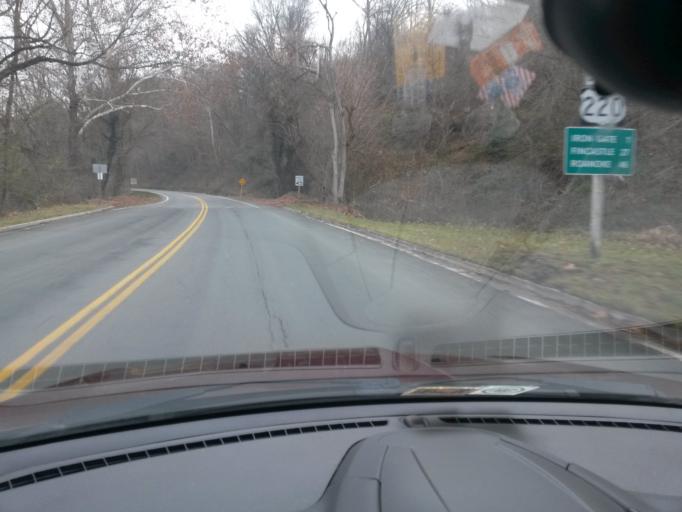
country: US
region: Virginia
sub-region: Alleghany County
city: Clifton Forge
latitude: 37.8106
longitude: -79.8128
